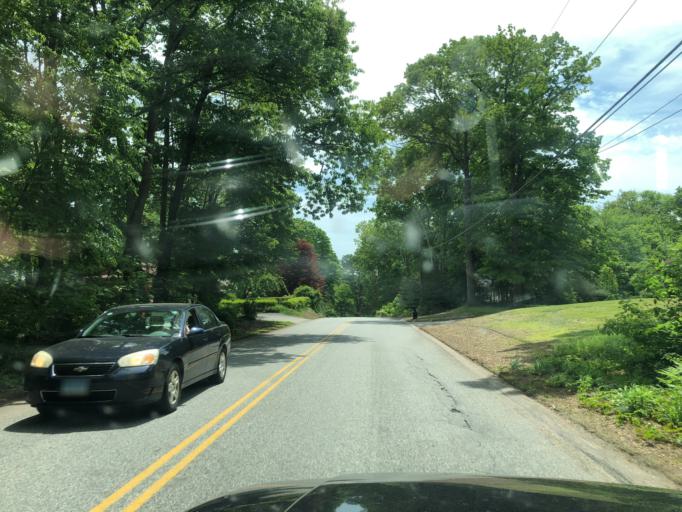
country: US
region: Connecticut
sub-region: Windham County
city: North Grosvenor Dale
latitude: 41.9782
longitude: -71.8890
